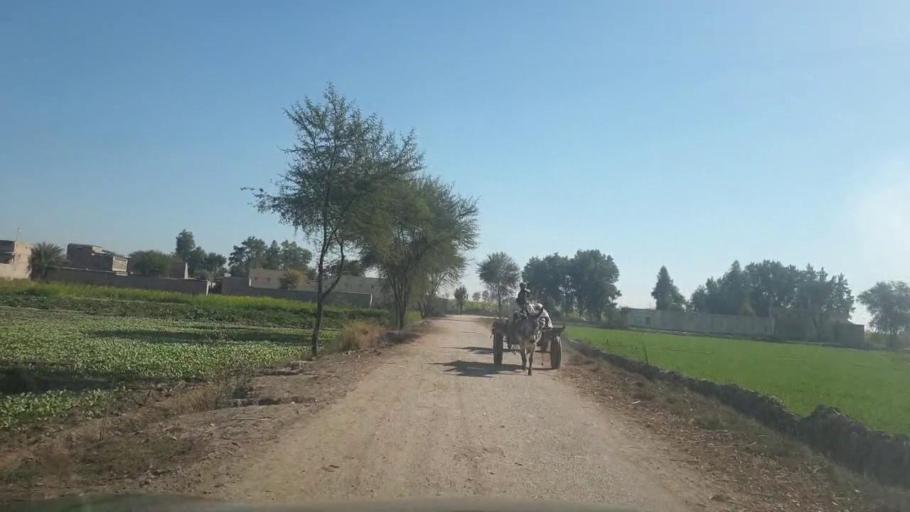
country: PK
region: Sindh
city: Adilpur
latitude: 27.9699
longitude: 69.3320
